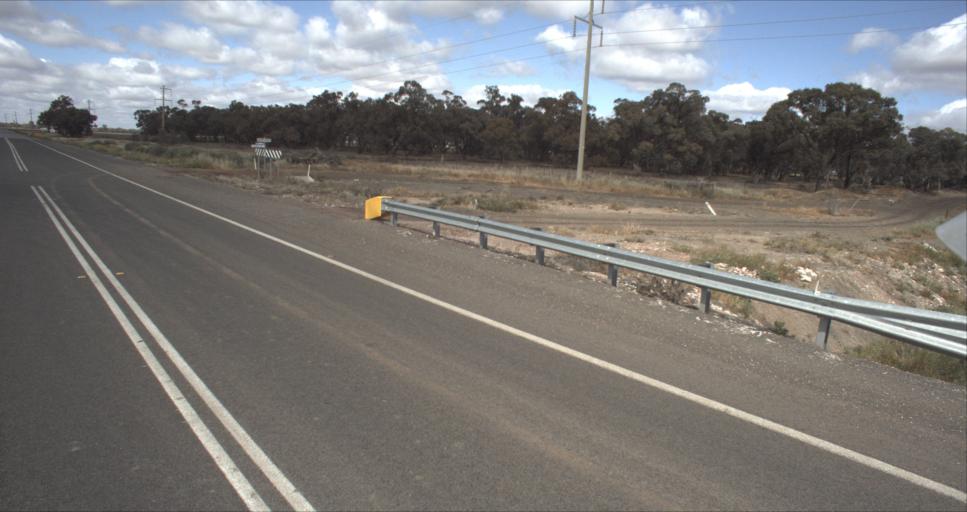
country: AU
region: New South Wales
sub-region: Murrumbidgee Shire
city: Darlington Point
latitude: -34.5743
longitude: 146.1665
